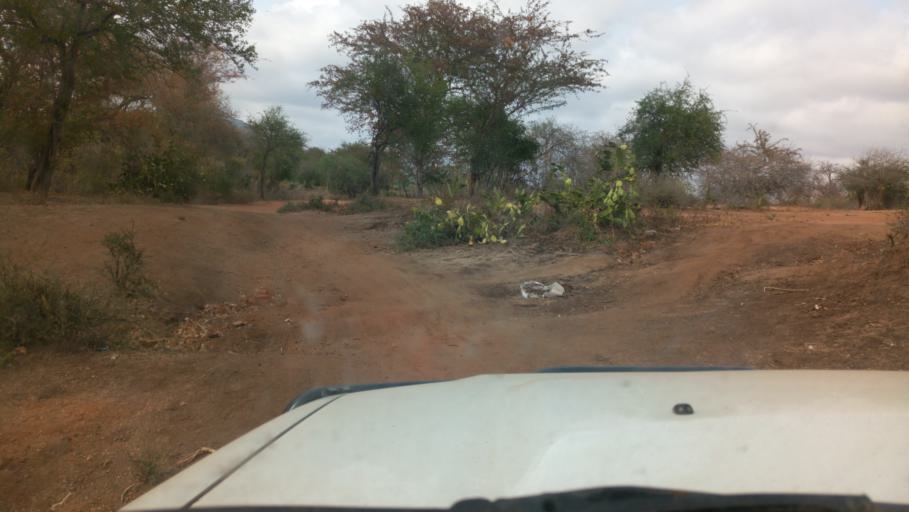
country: KE
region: Kitui
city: Kitui
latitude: -1.8575
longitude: 38.2824
